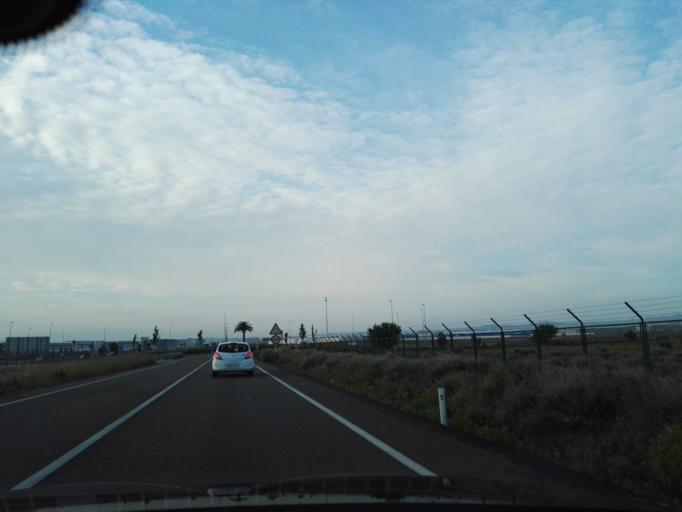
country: ES
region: Aragon
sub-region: Provincia de Zaragoza
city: Utebo
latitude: 41.6552
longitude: -1.0008
